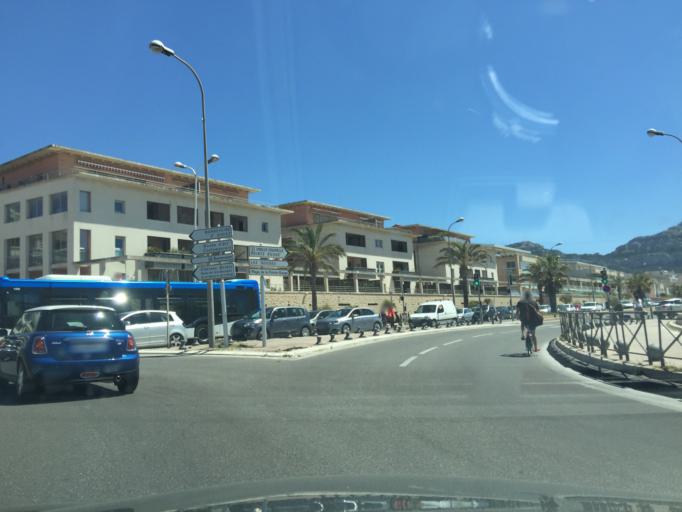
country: FR
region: Provence-Alpes-Cote d'Azur
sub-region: Departement des Bouches-du-Rhone
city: Marseille 08
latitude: 43.2545
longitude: 5.3759
